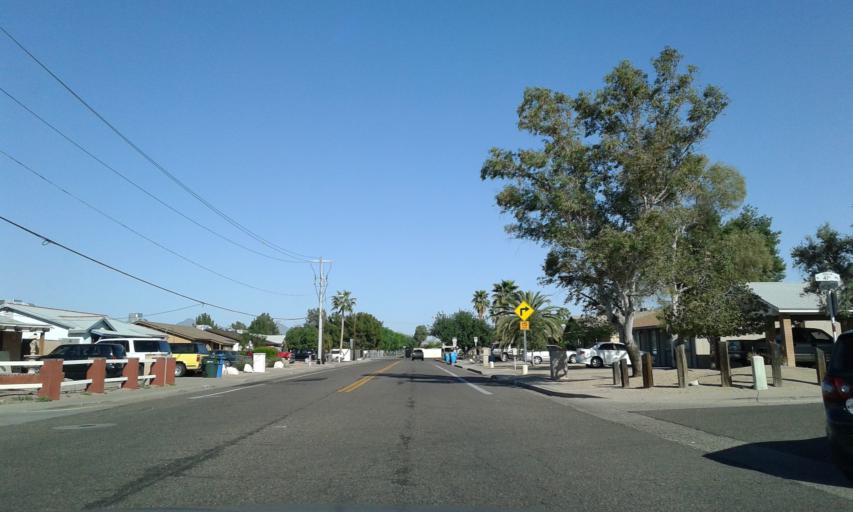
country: US
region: Arizona
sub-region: Maricopa County
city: Paradise Valley
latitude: 33.6044
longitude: -111.9926
